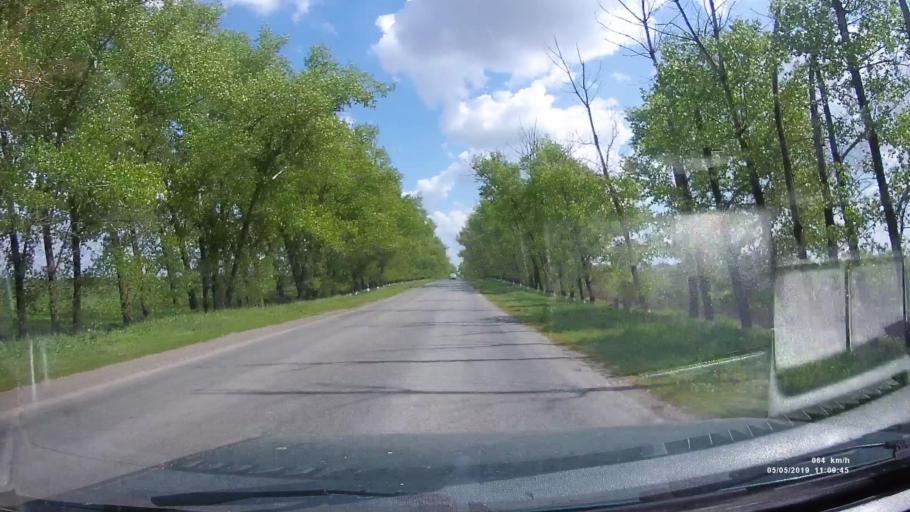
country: RU
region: Rostov
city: Ust'-Donetskiy
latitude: 47.7417
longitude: 40.9288
